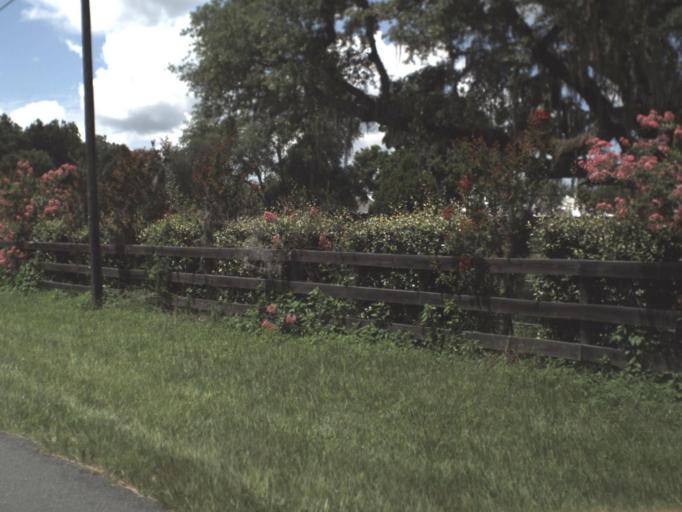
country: US
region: Florida
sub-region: Alachua County
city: Hawthorne
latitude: 29.6257
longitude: -82.0283
